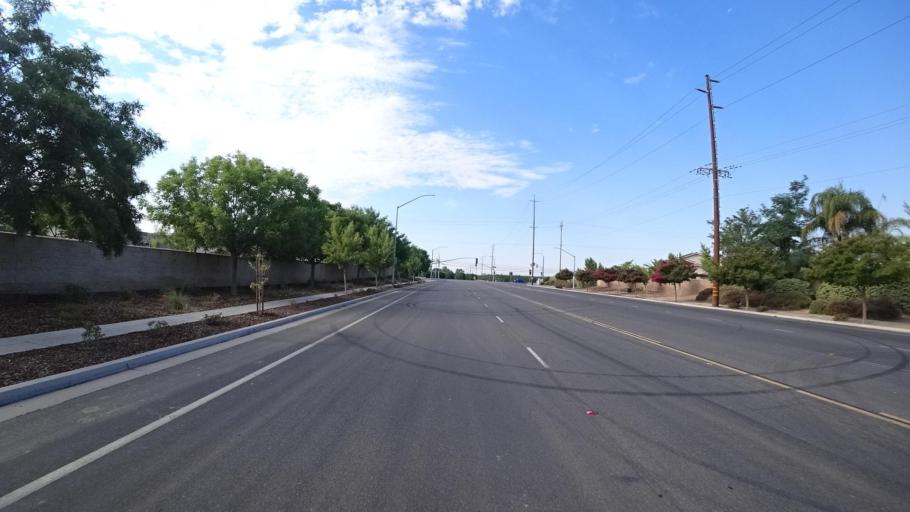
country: US
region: California
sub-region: Fresno County
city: Sunnyside
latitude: 36.7086
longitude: -119.6909
